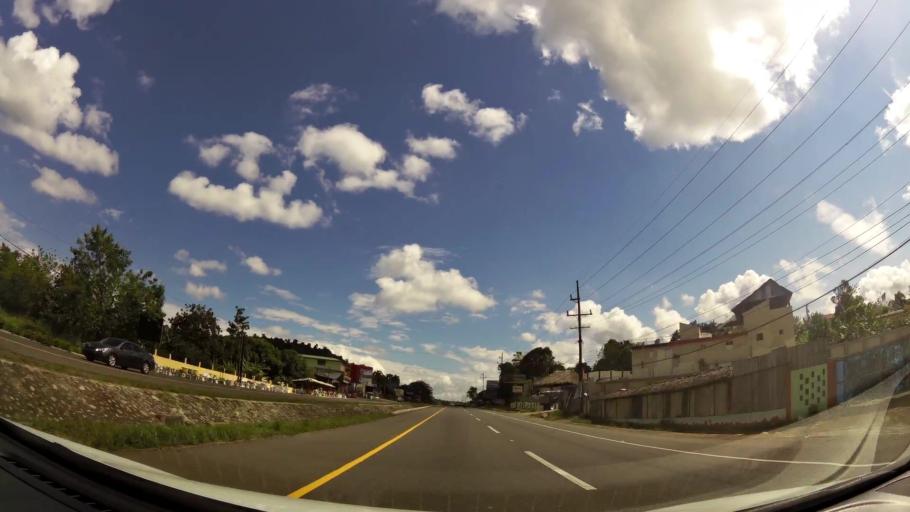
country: DO
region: La Vega
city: Rio Verde Arriba
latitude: 19.2882
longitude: -70.5746
